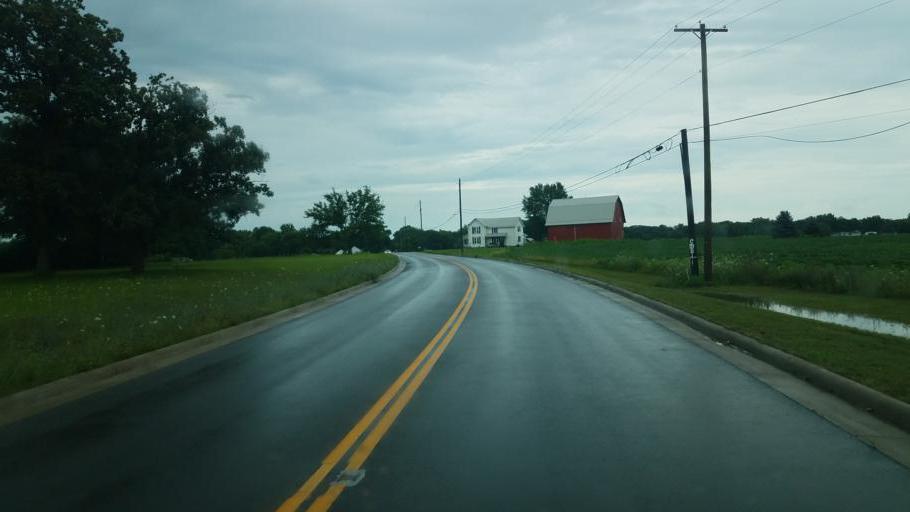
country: US
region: Ohio
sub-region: Marion County
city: Marion
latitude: 40.5711
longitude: -83.0924
